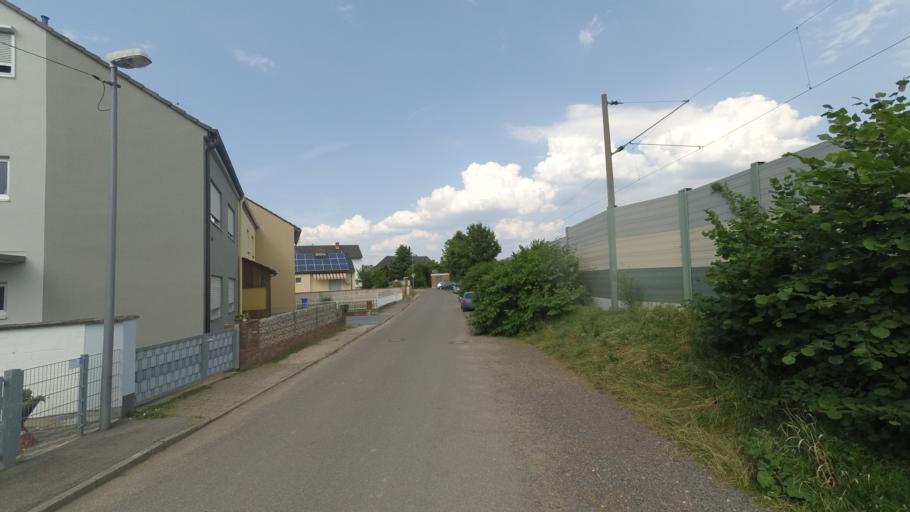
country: DE
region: Rheinland-Pfalz
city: Frankenthal
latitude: 49.5165
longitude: 8.3804
